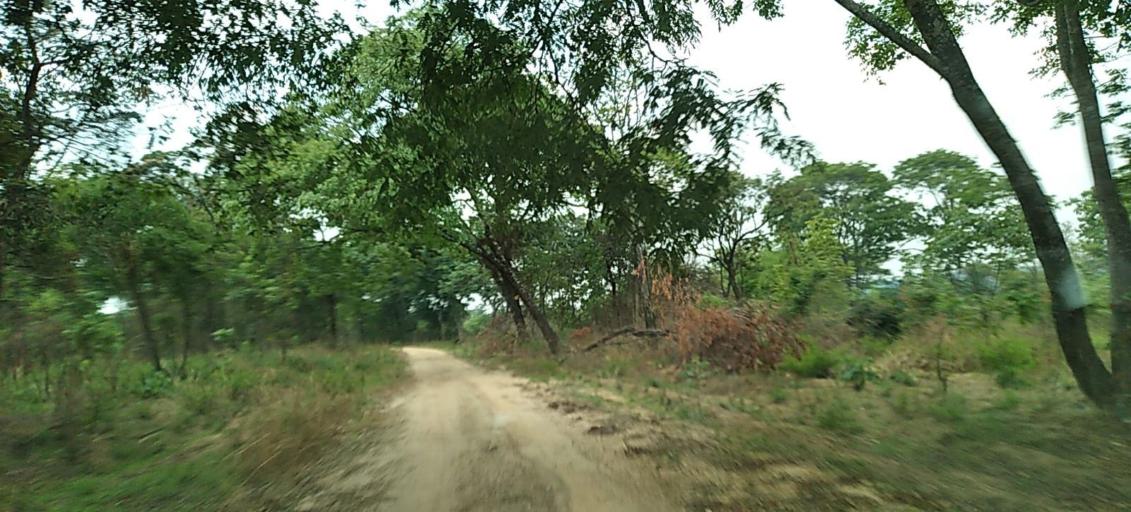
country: ZM
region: Copperbelt
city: Chingola
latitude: -12.7529
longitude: 27.7235
